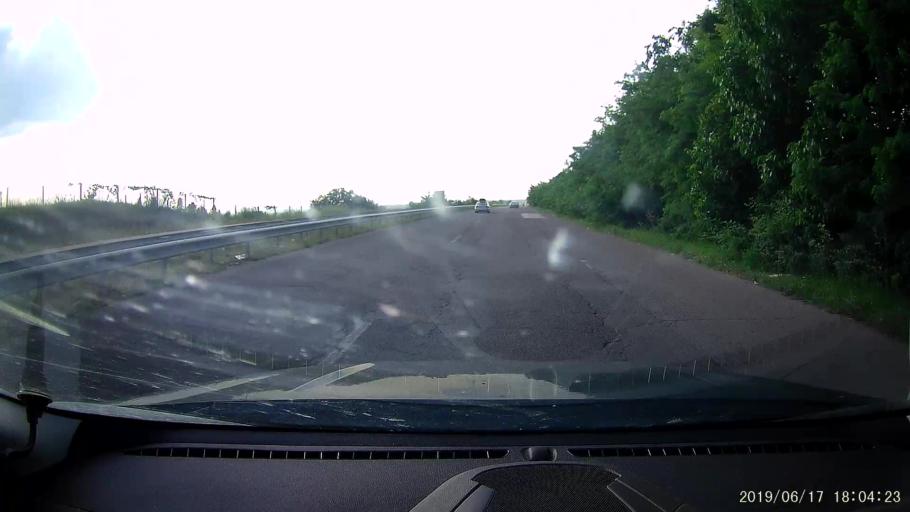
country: BG
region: Khaskovo
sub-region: Obshtina Svilengrad
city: Svilengrad
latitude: 41.7852
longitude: 26.1990
